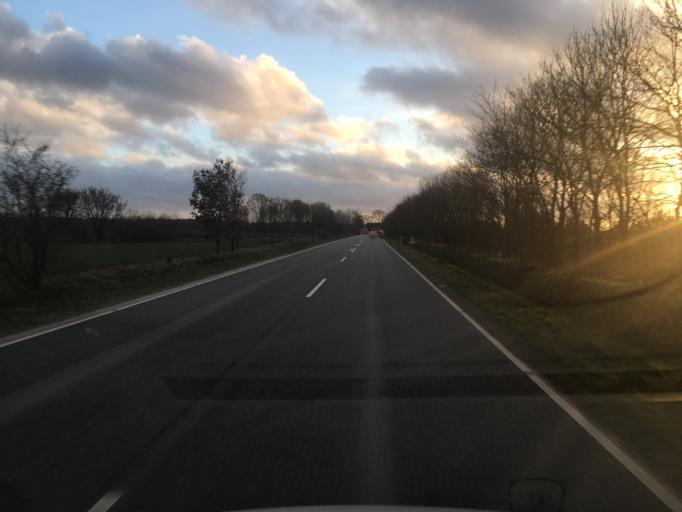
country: DK
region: South Denmark
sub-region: Aabenraa Kommune
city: Tinglev
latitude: 54.9574
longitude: 9.2871
